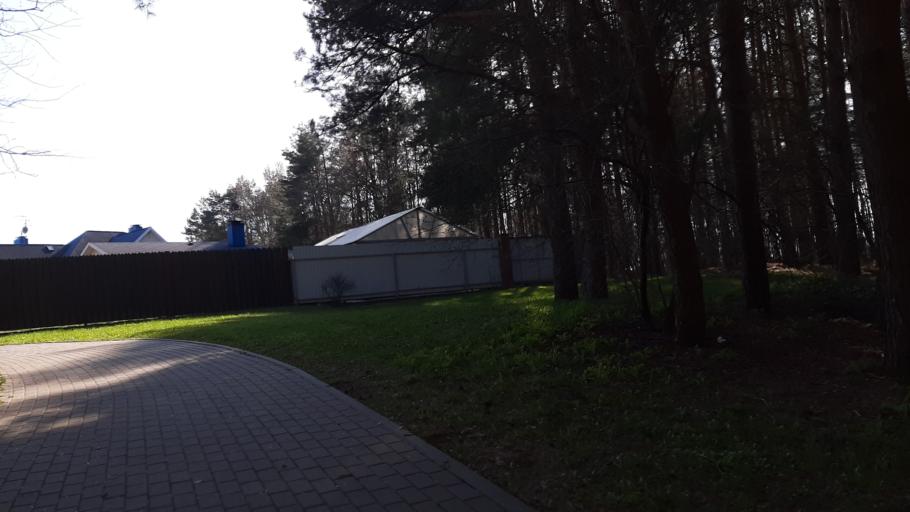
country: BY
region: Minsk
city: Bal'shavik
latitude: 53.9583
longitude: 27.5894
